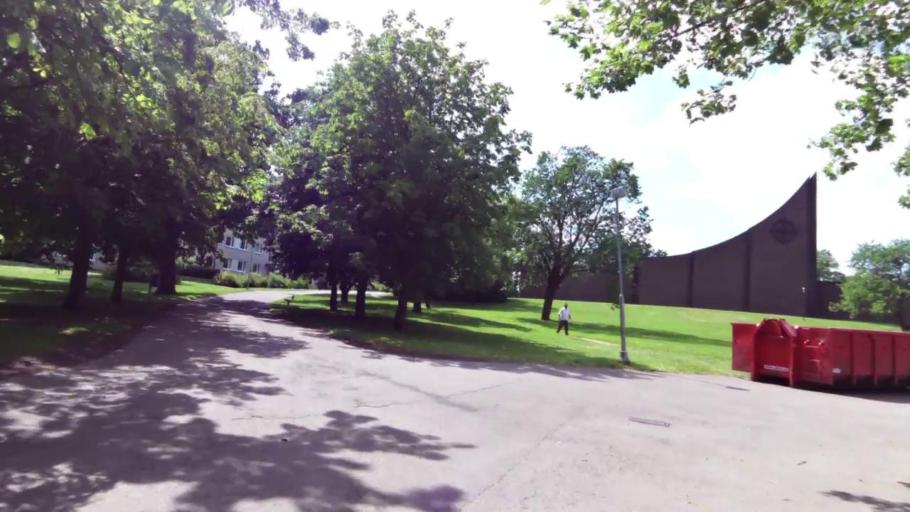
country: SE
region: OEstergoetland
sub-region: Linkopings Kommun
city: Linkoping
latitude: 58.4253
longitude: 15.5802
